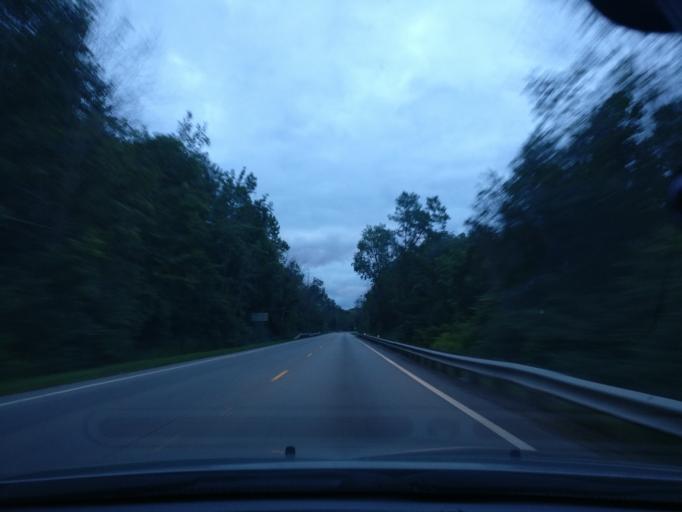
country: US
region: Ohio
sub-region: Warren County
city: Waynesville
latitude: 39.5290
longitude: -84.0926
